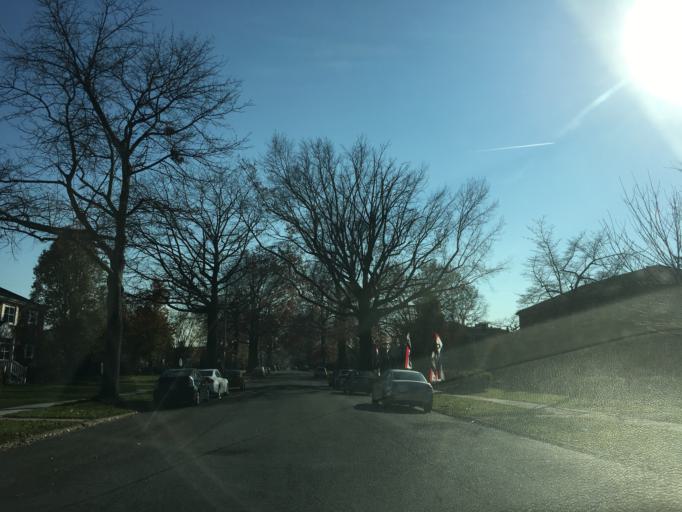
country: US
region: Pennsylvania
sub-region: Cumberland County
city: West Fairview
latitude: 40.2874
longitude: -76.9012
